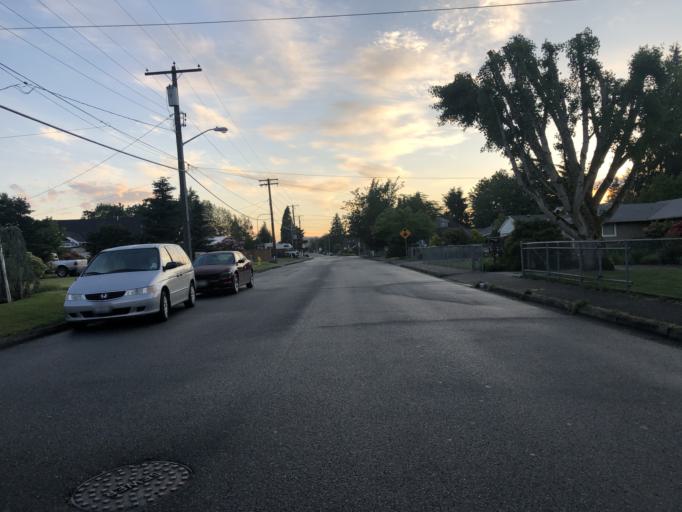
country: US
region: Washington
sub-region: King County
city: Auburn
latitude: 47.3082
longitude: -122.2062
